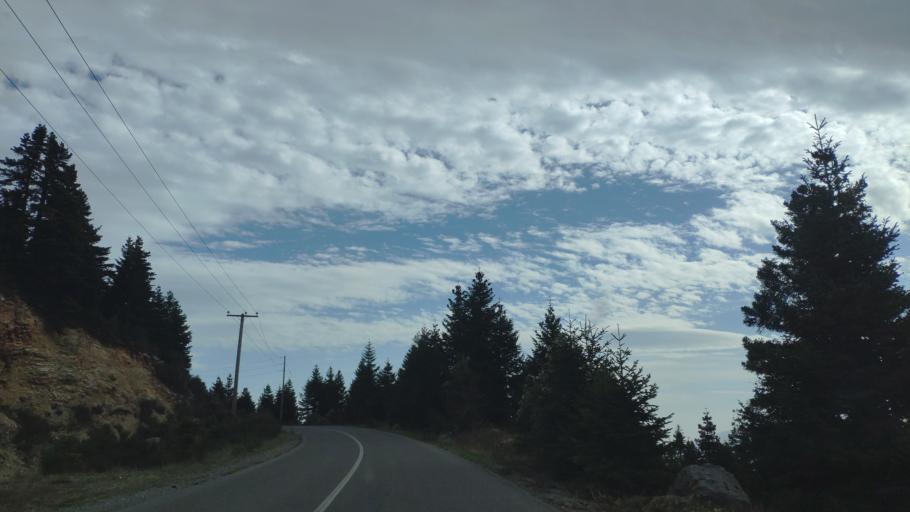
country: GR
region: Central Greece
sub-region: Nomos Fokidos
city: Amfissa
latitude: 38.7025
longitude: 22.3178
